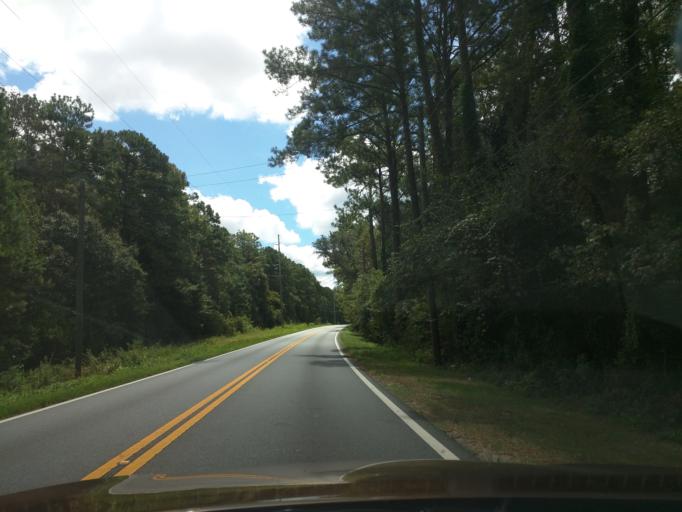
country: US
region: Florida
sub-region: Leon County
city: Tallahassee
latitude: 30.5772
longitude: -84.2339
